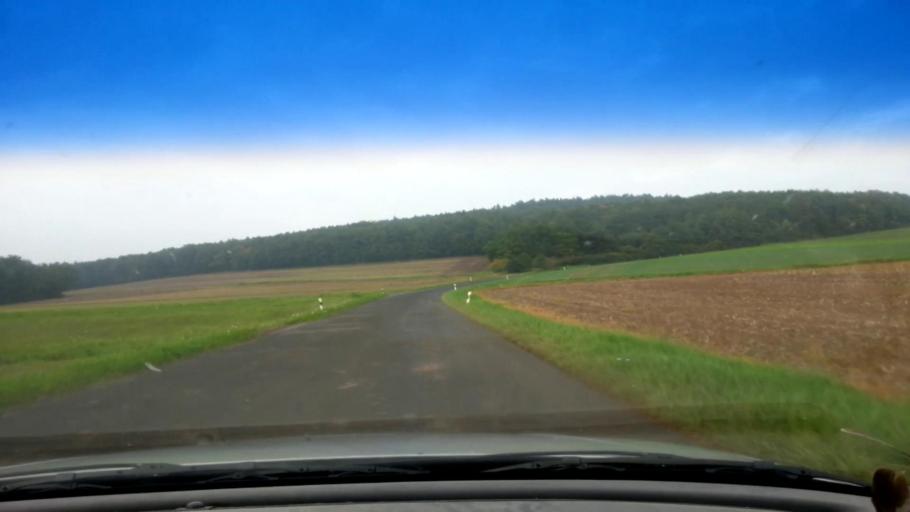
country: DE
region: Bavaria
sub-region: Upper Franconia
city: Rattelsdorf
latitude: 50.0566
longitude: 10.8880
